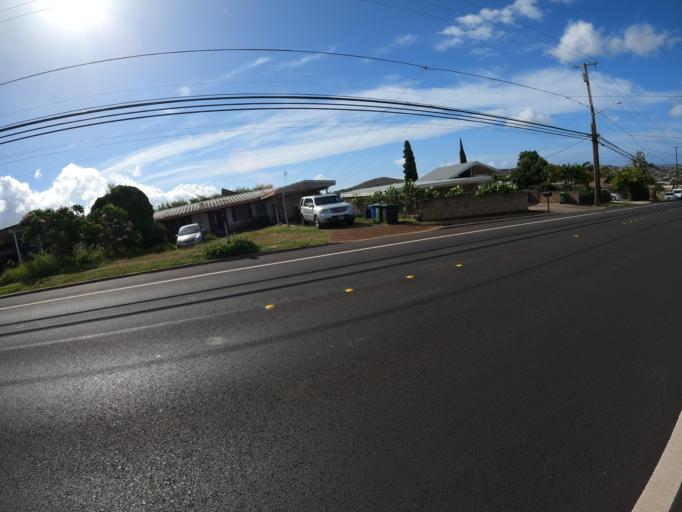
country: US
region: Hawaii
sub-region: Honolulu County
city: Halawa Heights
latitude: 21.3776
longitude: -157.9164
